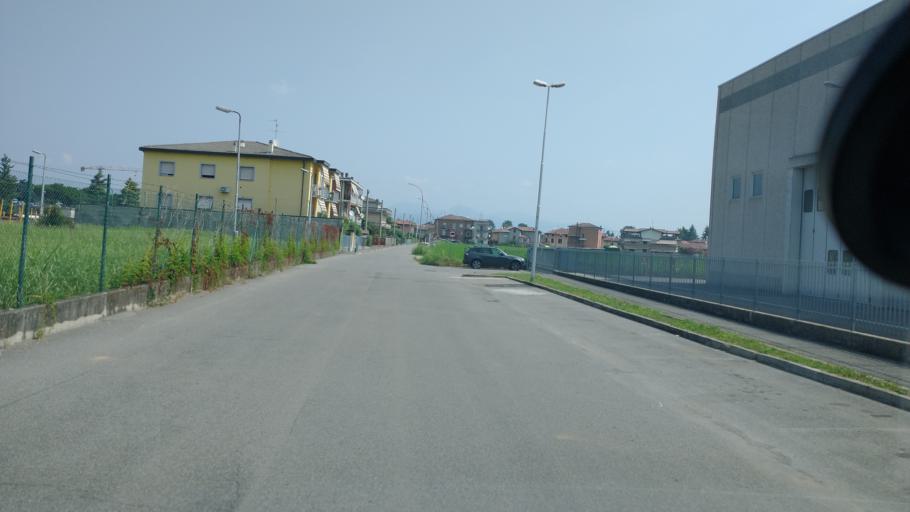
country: IT
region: Lombardy
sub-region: Provincia di Bergamo
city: Levate
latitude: 45.6351
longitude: 9.6143
